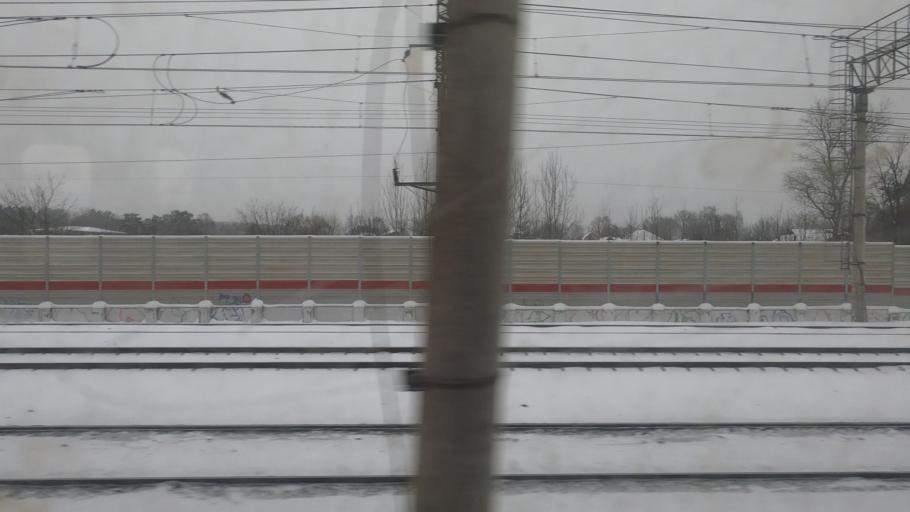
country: RU
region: Moskovskaya
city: Reutov
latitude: 55.7587
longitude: 37.8926
